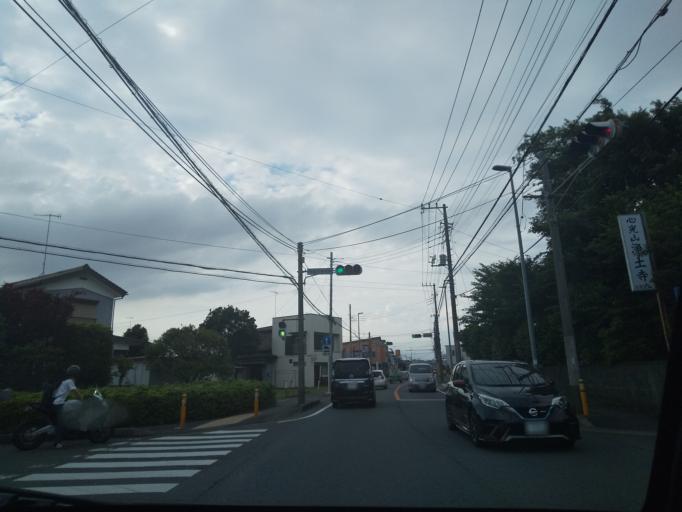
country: JP
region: Kanagawa
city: Zama
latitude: 35.4741
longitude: 139.3887
